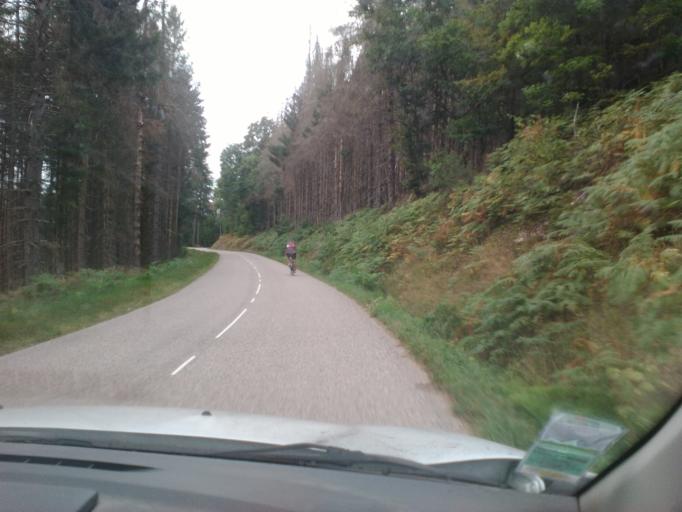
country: FR
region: Lorraine
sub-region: Departement des Vosges
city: Le Tholy
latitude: 48.1044
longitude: 6.7600
